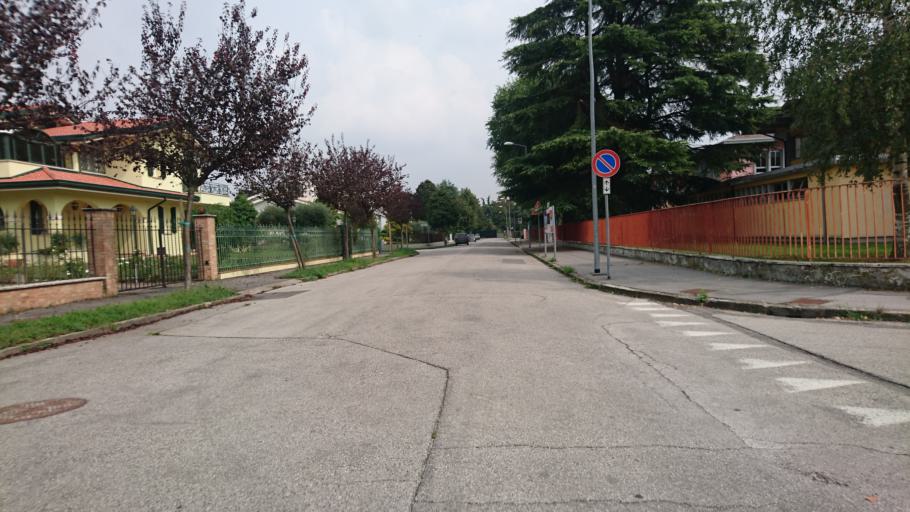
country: IT
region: Veneto
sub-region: Provincia di Padova
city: Tencarola
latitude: 45.3898
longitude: 11.8130
